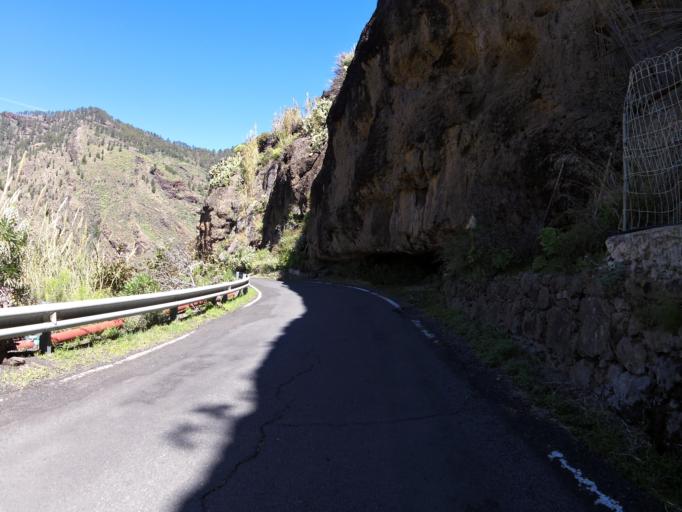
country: ES
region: Canary Islands
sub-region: Provincia de Las Palmas
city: Artenara
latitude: 28.0081
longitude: -15.6897
